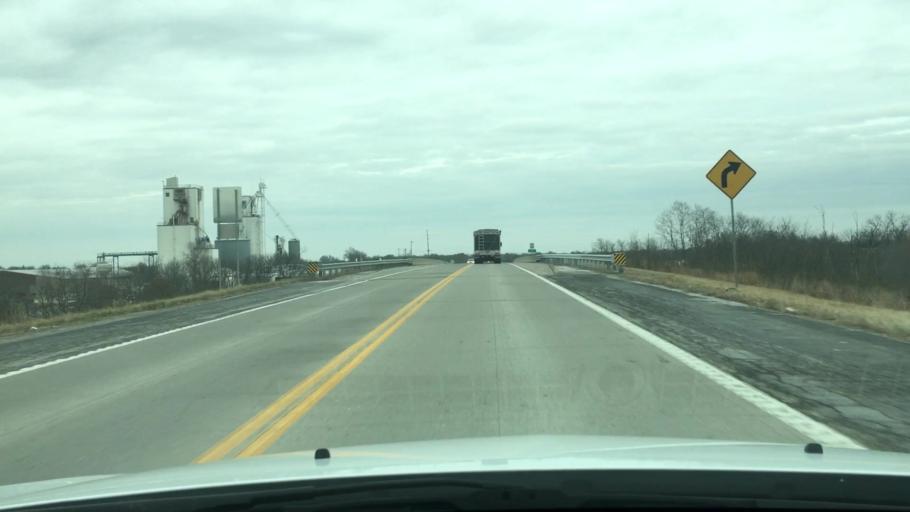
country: US
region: Missouri
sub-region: Audrain County
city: Mexico
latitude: 39.1560
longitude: -91.8430
